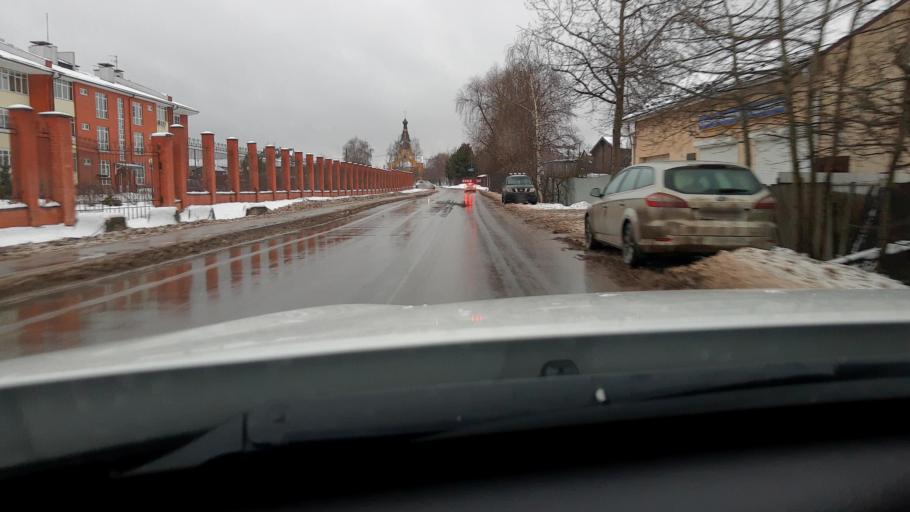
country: RU
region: Moskovskaya
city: Krasnogorsk
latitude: 55.8609
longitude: 37.3190
